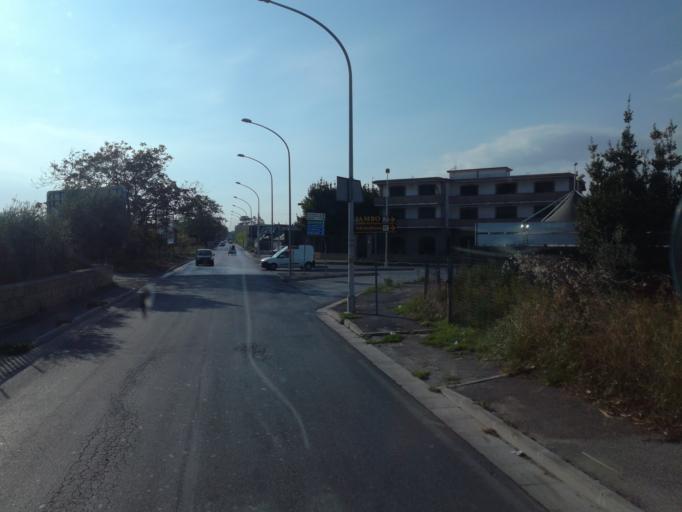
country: IT
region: Campania
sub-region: Provincia di Napoli
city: Giugliano in Campania
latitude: 40.9397
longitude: 14.1844
